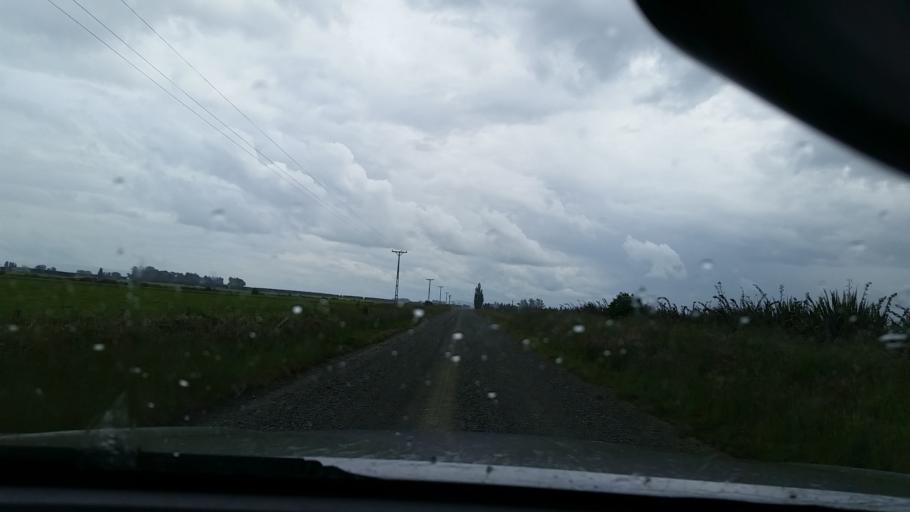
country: NZ
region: Southland
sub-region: Southland District
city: Winton
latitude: -46.0067
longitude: 168.2388
